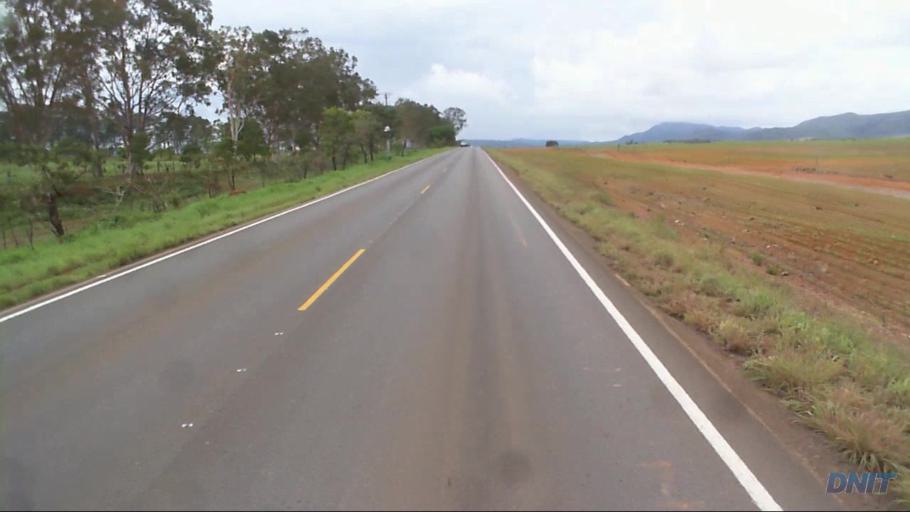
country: BR
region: Goias
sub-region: Padre Bernardo
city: Padre Bernardo
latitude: -15.3165
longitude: -48.2288
